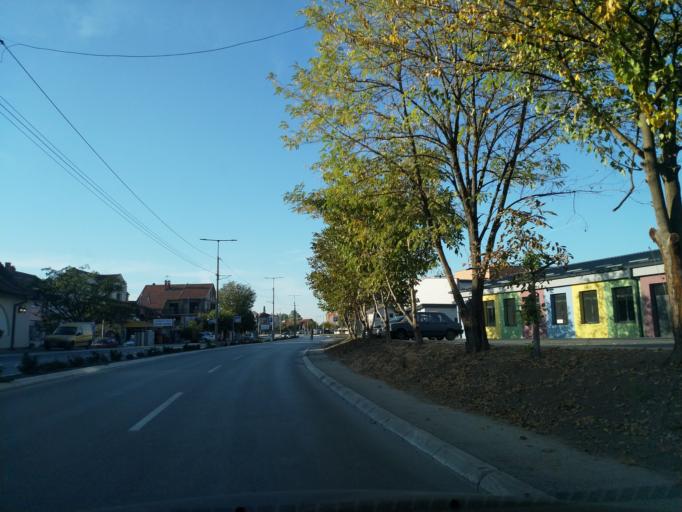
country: RS
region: Central Serbia
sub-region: Pomoravski Okrug
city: Svilajnac
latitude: 44.2305
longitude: 21.1929
